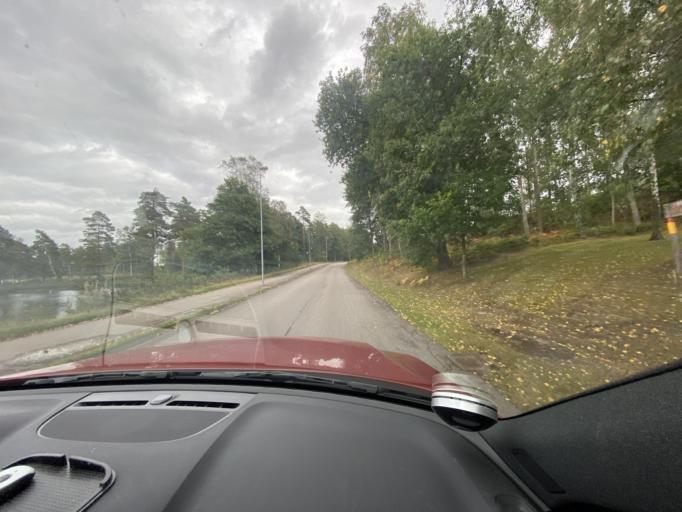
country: SE
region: Kronoberg
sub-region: Markaryds Kommun
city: Markaryd
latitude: 56.4609
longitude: 13.6075
